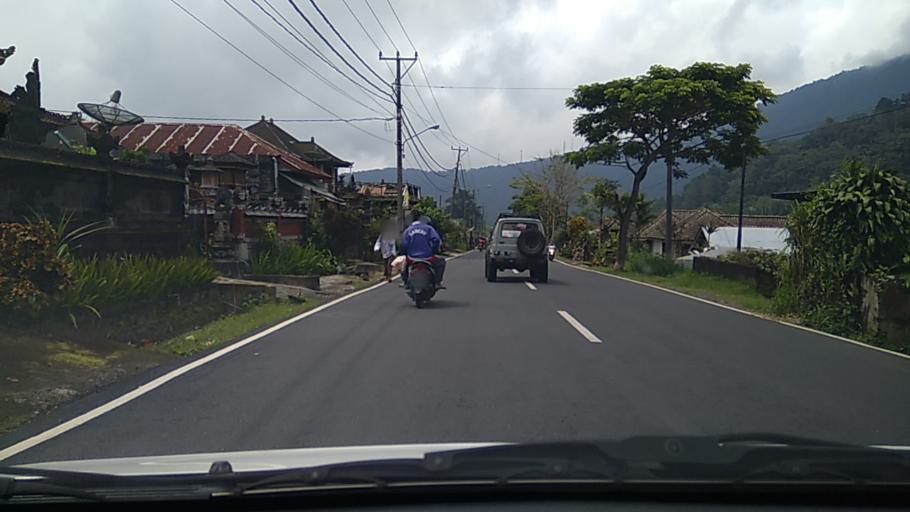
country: ID
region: Bali
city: Munduk
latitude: -8.2606
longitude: 115.1633
